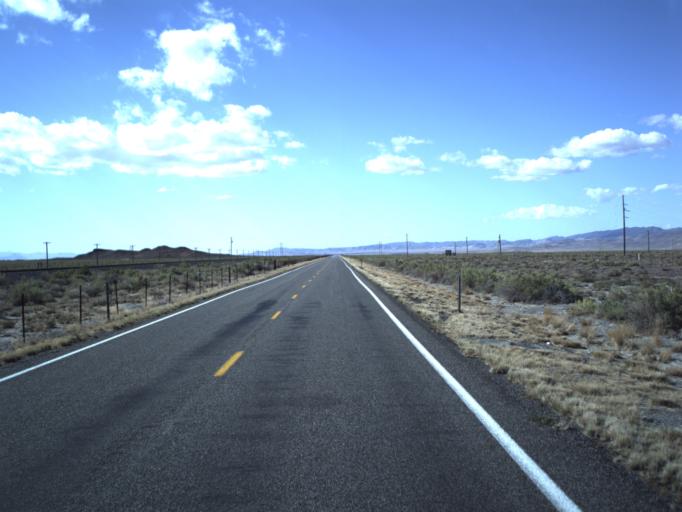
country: US
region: Utah
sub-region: Millard County
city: Delta
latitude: 39.1622
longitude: -112.7117
